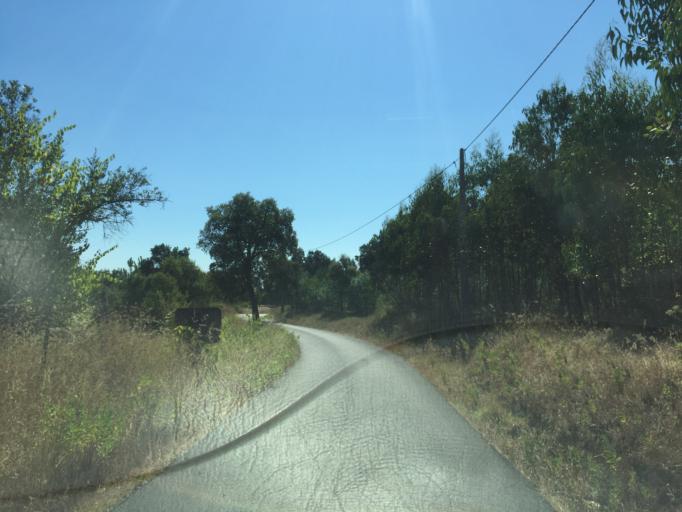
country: PT
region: Santarem
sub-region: Ferreira do Zezere
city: Ferreira do Zezere
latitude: 39.5938
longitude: -8.2898
